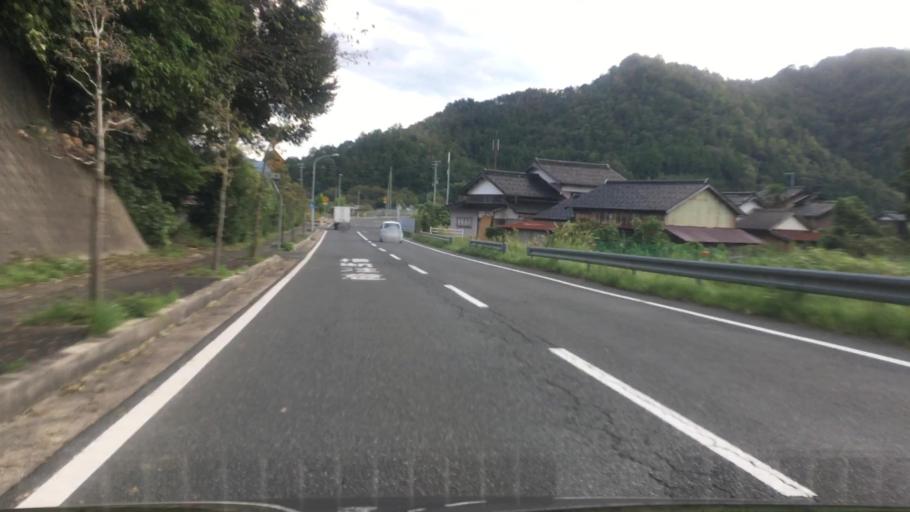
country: JP
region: Hyogo
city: Toyooka
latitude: 35.6112
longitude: 134.9191
